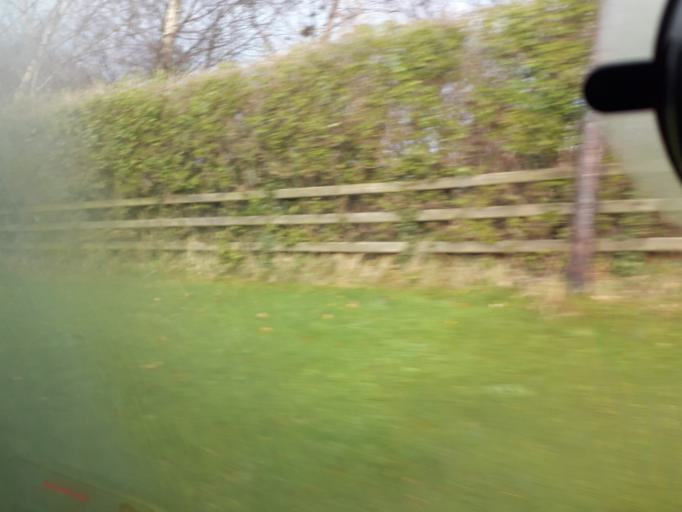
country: IE
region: Leinster
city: Ballyboden
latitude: 53.2490
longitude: -6.2999
